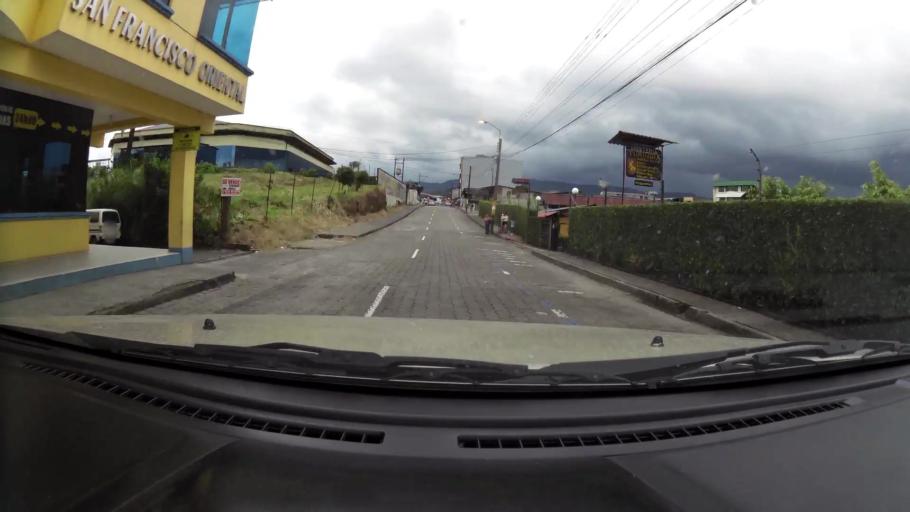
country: EC
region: Pastaza
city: Puyo
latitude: -1.4867
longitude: -78.0013
